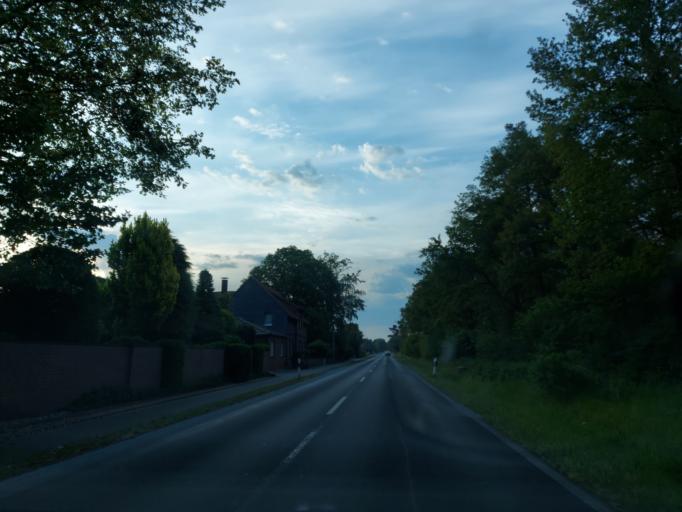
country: DE
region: North Rhine-Westphalia
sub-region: Regierungsbezirk Detmold
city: Verl
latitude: 51.9361
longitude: 8.4609
